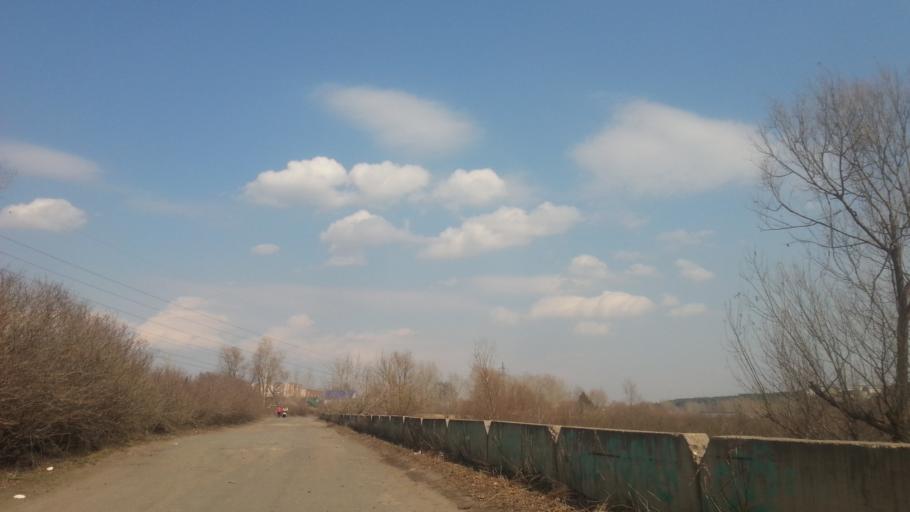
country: RU
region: Altai Krai
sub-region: Gorod Barnaulskiy
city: Barnaul
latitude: 53.3107
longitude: 83.7244
